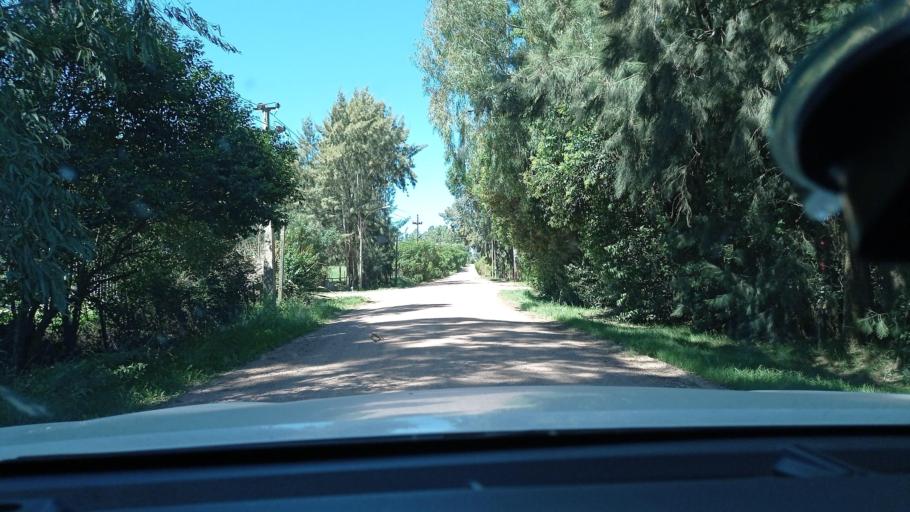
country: UY
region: Canelones
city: La Paz
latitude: -34.7603
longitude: -56.1779
